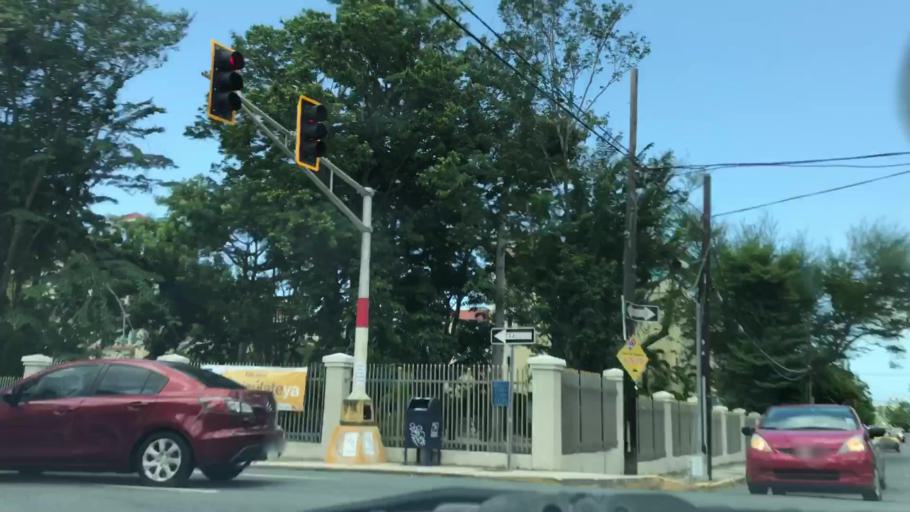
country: PR
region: Catano
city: Catano
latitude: 18.4213
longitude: -66.0568
